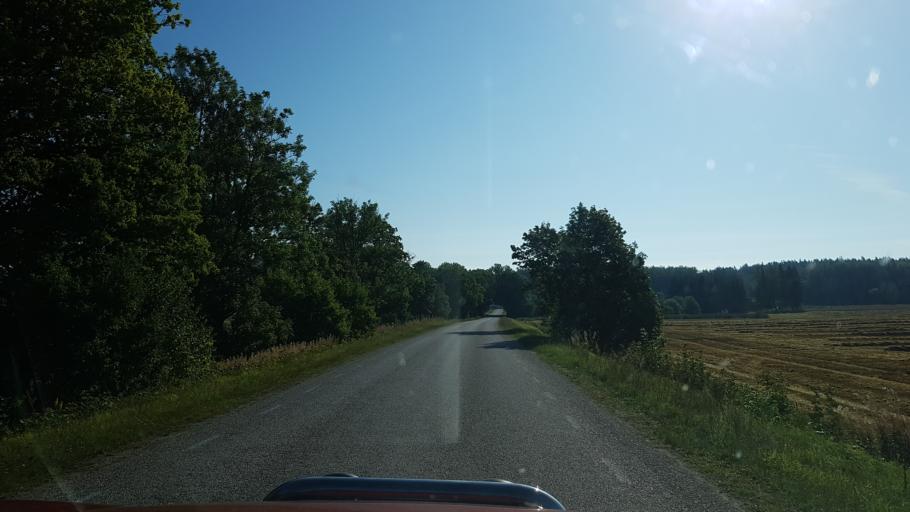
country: EE
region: Jogevamaa
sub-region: Tabivere vald
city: Tabivere
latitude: 58.6694
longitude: 26.7623
